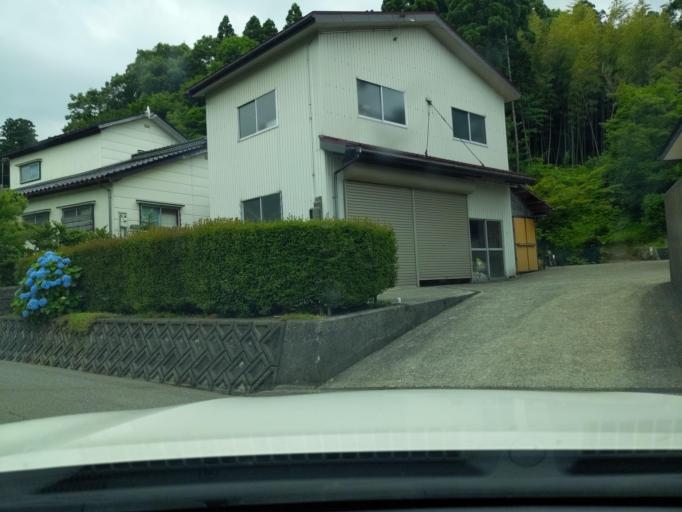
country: JP
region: Niigata
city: Kashiwazaki
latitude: 37.3419
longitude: 138.5885
